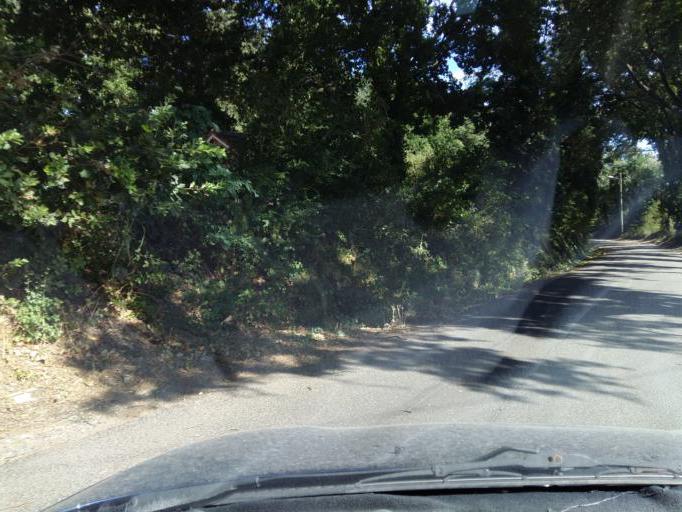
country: FR
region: Provence-Alpes-Cote d'Azur
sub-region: Departement du Vaucluse
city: Piolenc
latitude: 44.1848
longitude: 4.7588
